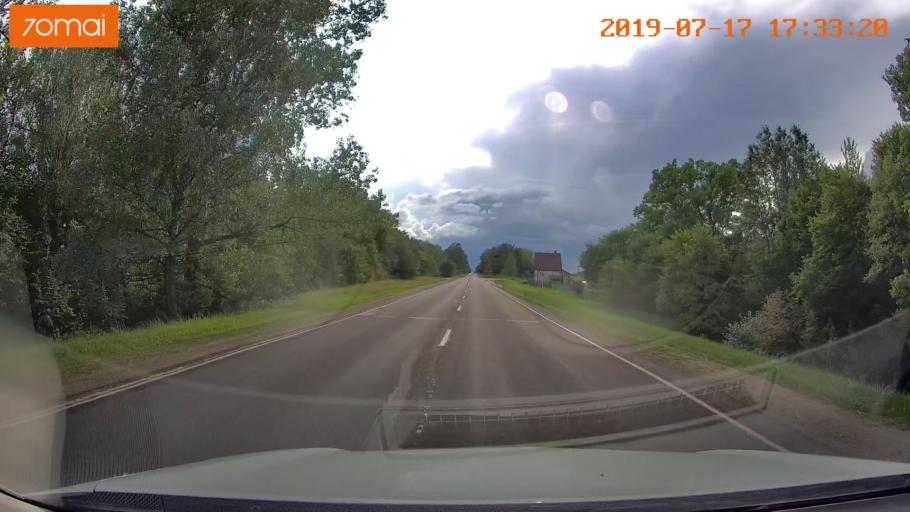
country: BY
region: Mogilev
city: Babruysk
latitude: 53.1117
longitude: 29.0946
